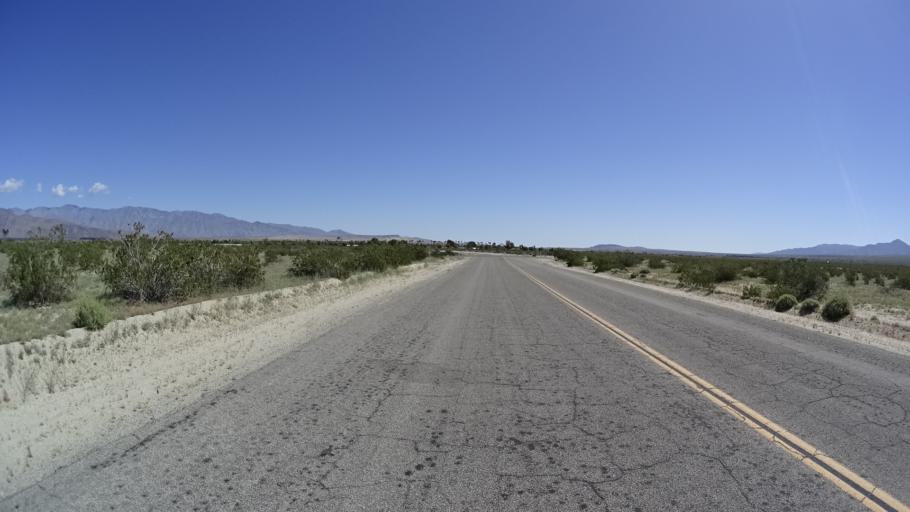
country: US
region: California
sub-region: San Diego County
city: Borrego Springs
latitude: 33.2315
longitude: -116.3667
